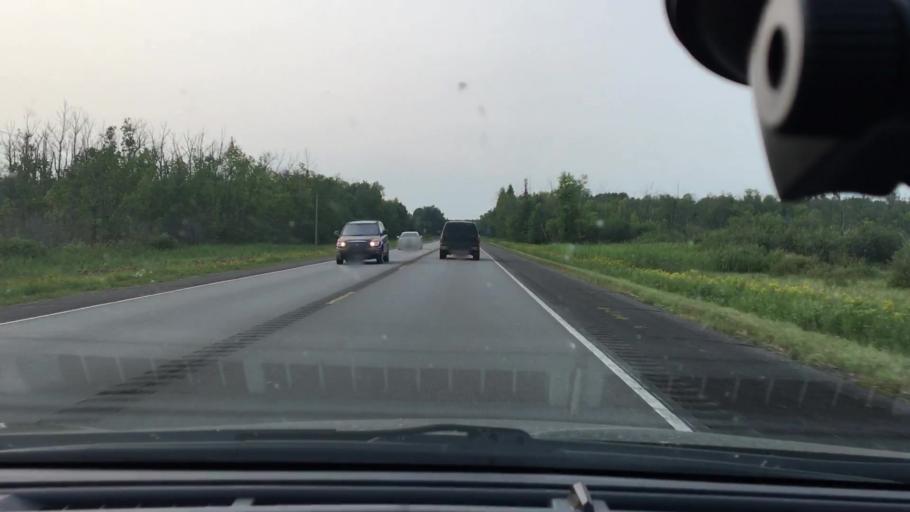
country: US
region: Minnesota
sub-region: Mille Lacs County
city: Vineland
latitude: 46.3184
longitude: -93.8381
